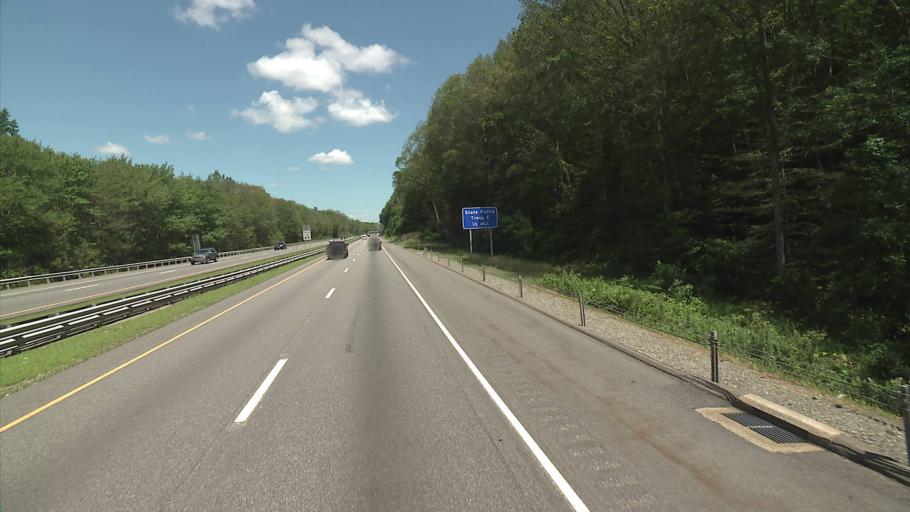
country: US
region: Connecticut
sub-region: New London County
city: Oxoboxo River
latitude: 41.4654
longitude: -72.1156
